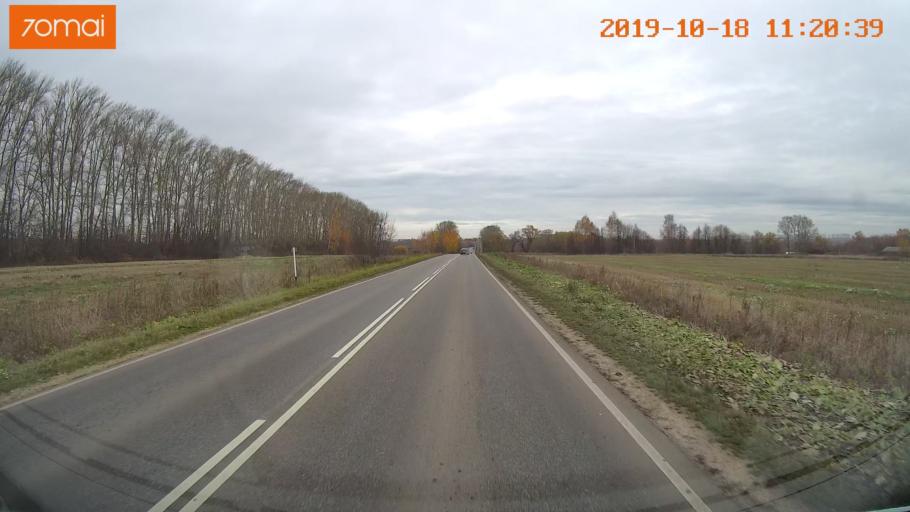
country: RU
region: Tula
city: Kimovsk
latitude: 54.0639
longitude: 38.5597
